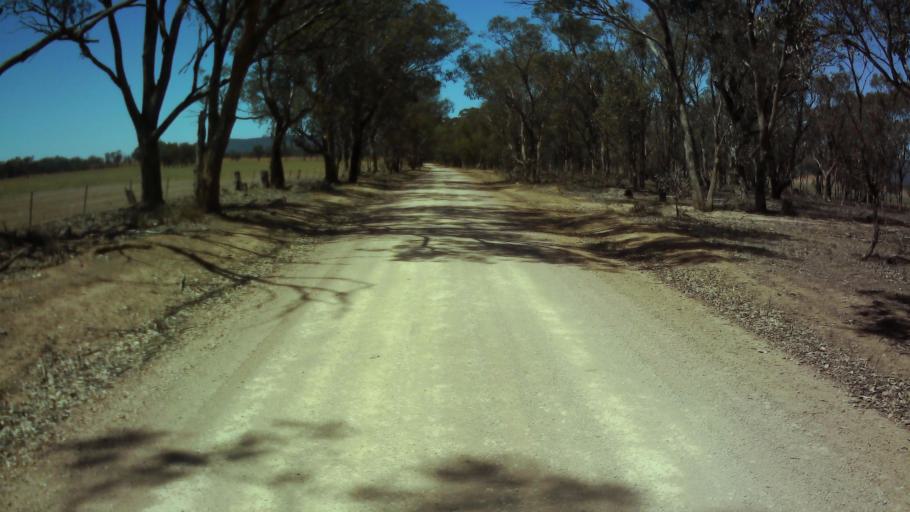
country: AU
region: New South Wales
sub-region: Weddin
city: Grenfell
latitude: -33.9234
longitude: 148.0784
